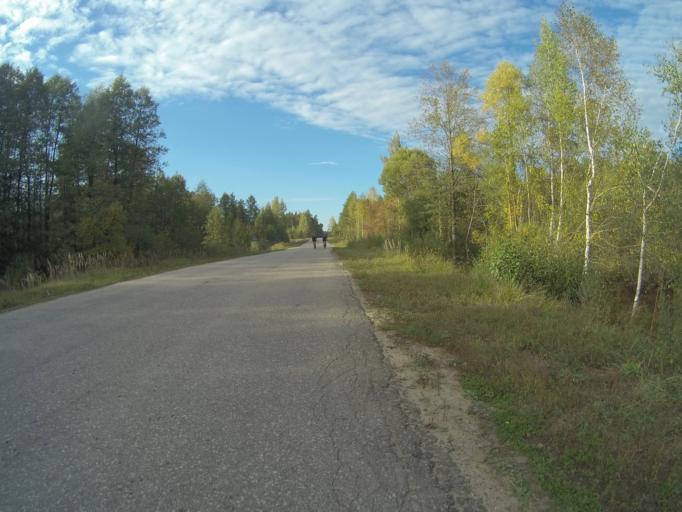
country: RU
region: Vladimir
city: Sobinka
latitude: 55.9184
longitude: 40.0017
